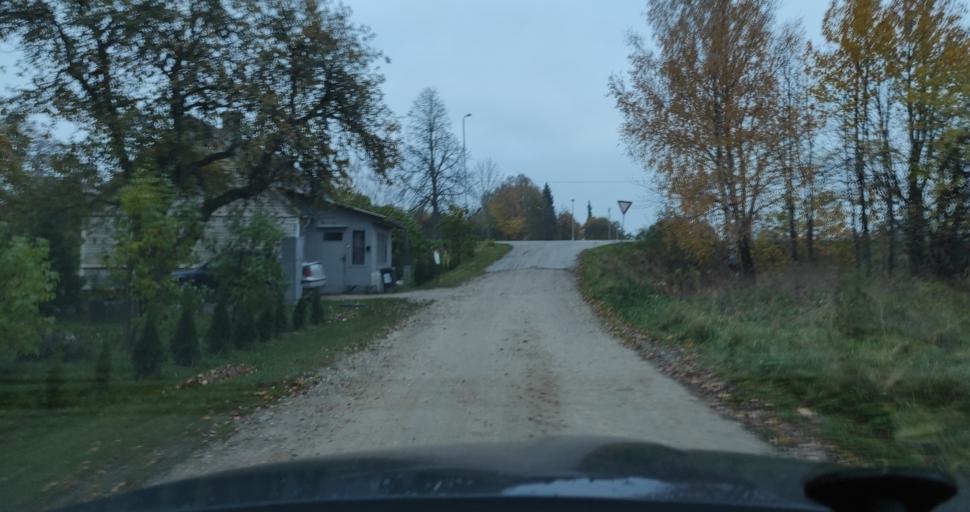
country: LV
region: Aizpute
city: Aizpute
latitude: 56.7183
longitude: 21.5832
